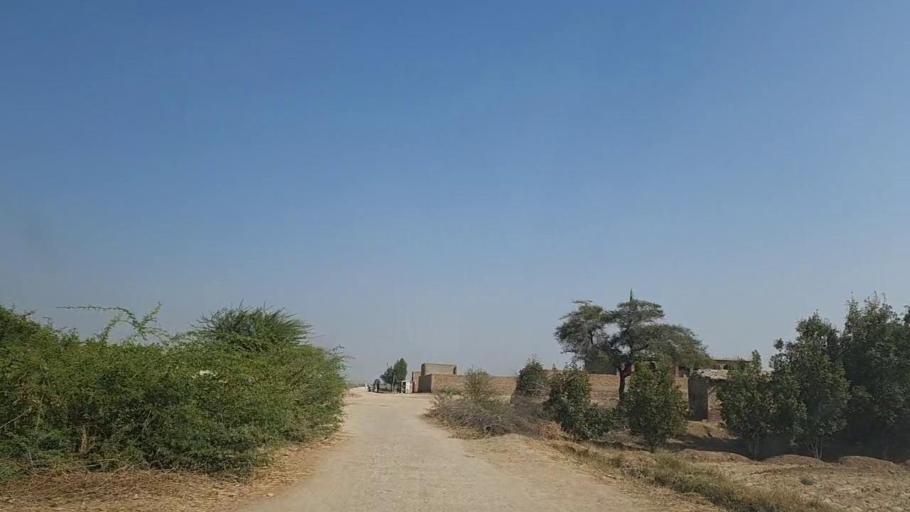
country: PK
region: Sindh
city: Naukot
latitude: 24.8992
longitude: 69.4545
